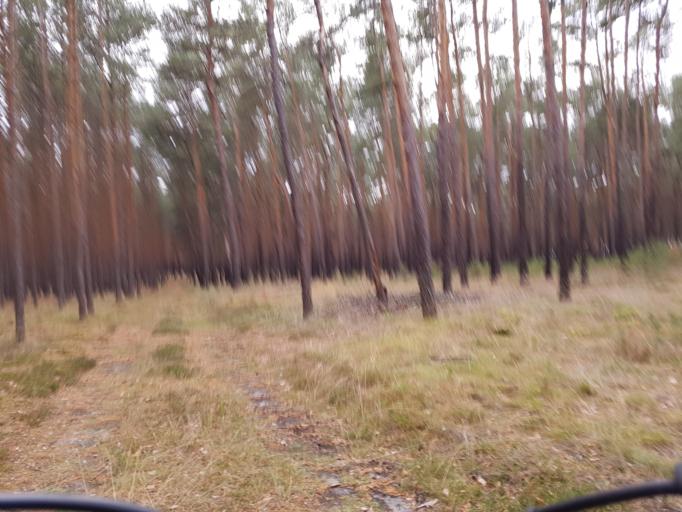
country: DE
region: Brandenburg
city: Schilda
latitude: 51.6164
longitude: 13.3808
